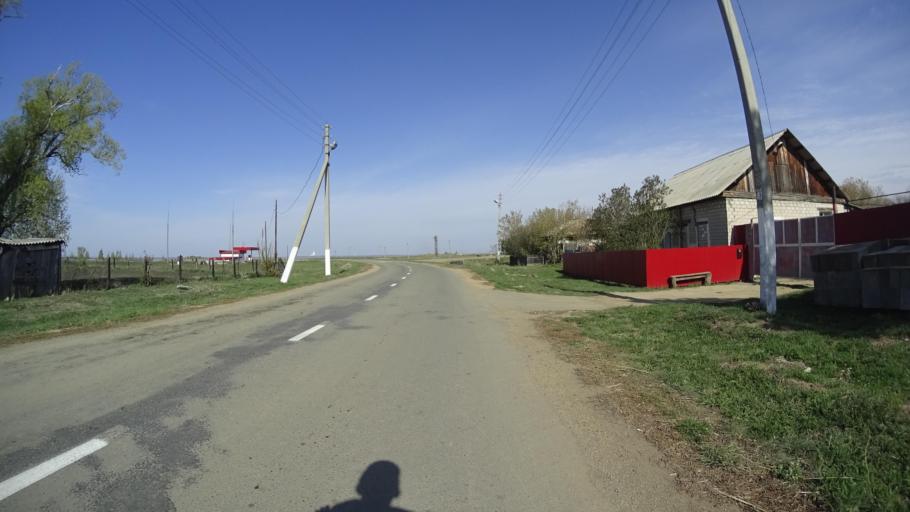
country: RU
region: Chelyabinsk
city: Chesma
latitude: 53.8023
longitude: 61.0176
